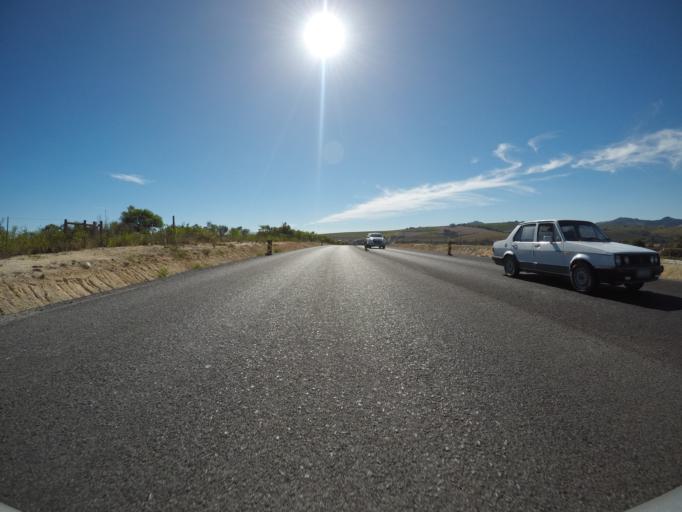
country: ZA
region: Western Cape
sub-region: Cape Winelands District Municipality
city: Stellenbosch
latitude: -33.9893
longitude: 18.7869
